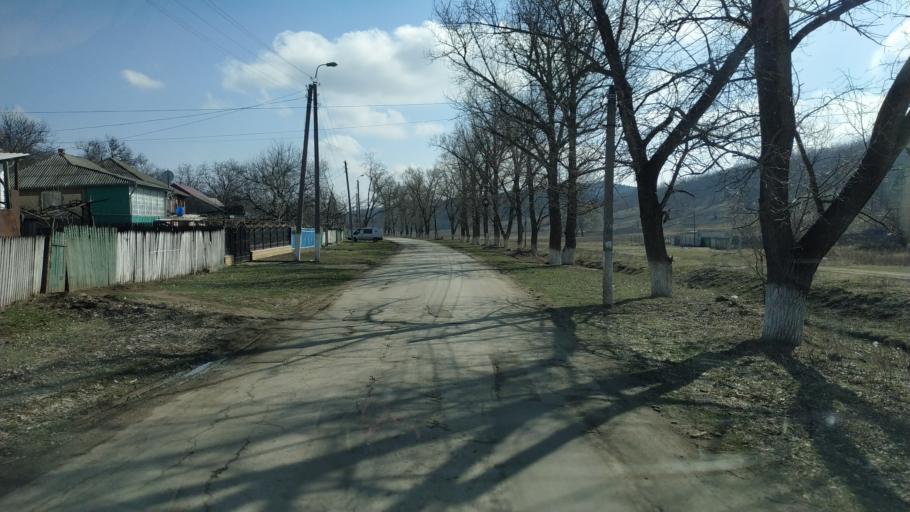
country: MD
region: Hincesti
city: Hincesti
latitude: 46.8748
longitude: 28.6306
